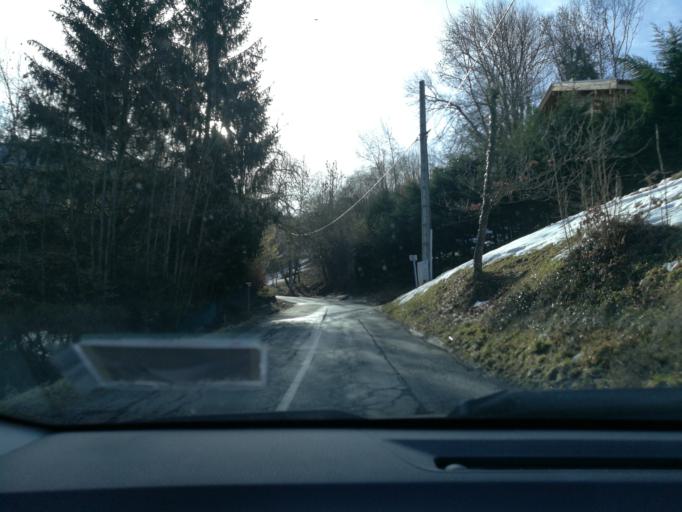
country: FR
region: Rhone-Alpes
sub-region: Departement de la Haute-Savoie
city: Saint-Gervais-les-Bains
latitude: 45.9006
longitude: 6.6999
